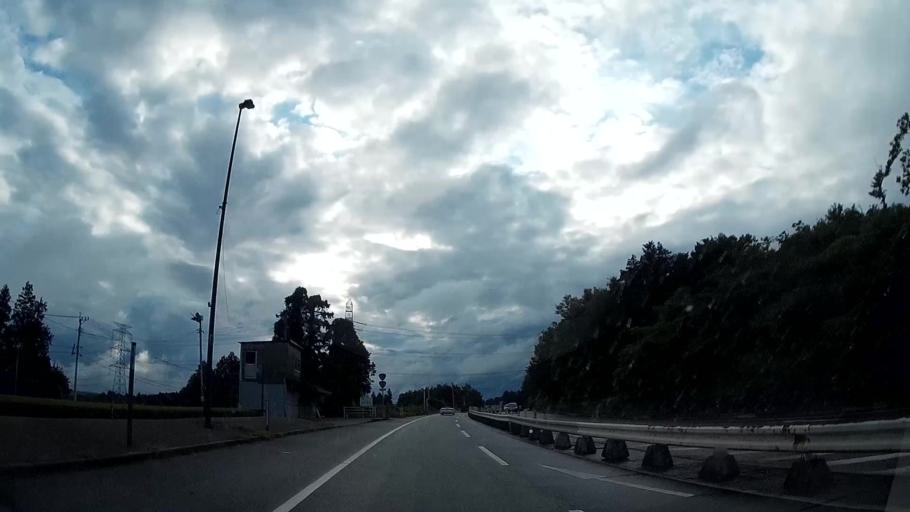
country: JP
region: Kumamoto
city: Ozu
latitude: 32.8759
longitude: 130.9270
